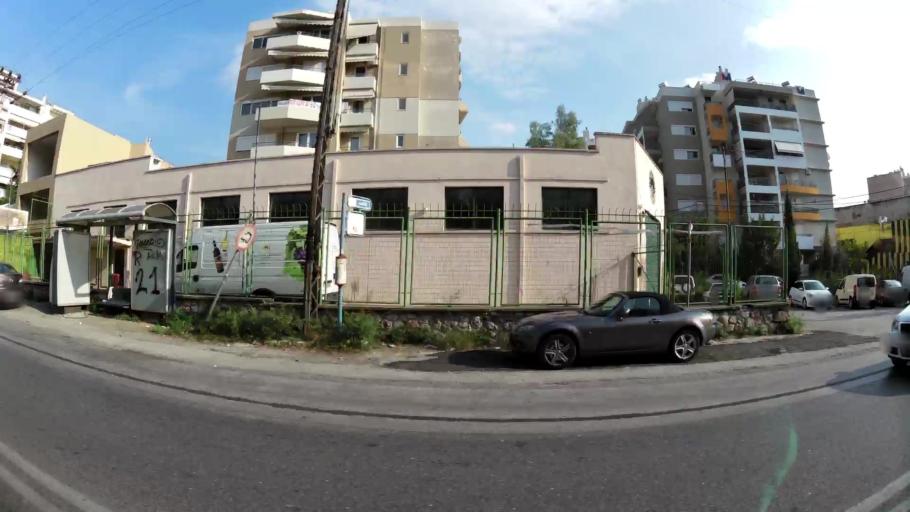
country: GR
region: Attica
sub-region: Nomarchia Athinas
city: Nea Filadelfeia
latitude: 38.0383
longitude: 23.7444
